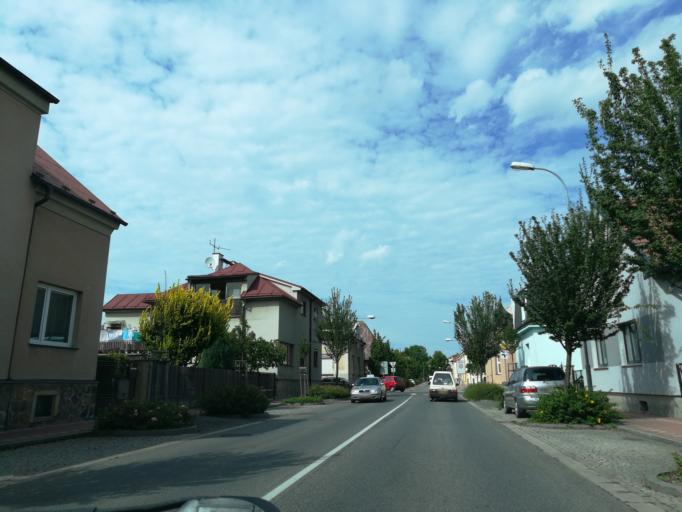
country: CZ
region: Kralovehradecky
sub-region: Okres Jicin
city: Jicin
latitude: 50.4367
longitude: 15.3620
